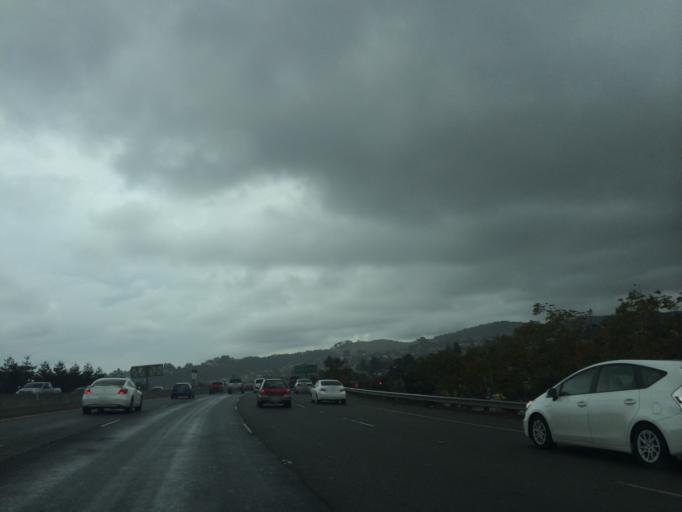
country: US
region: California
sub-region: Contra Costa County
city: East Richmond Heights
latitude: 37.9358
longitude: -122.3267
